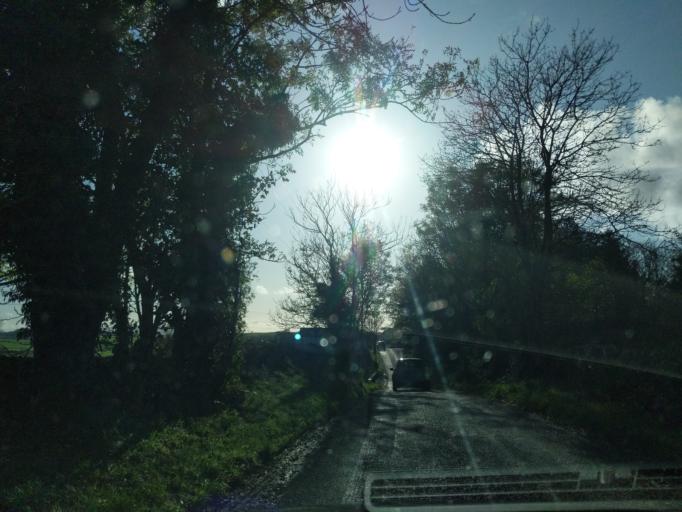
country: GB
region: Scotland
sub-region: Dumfries and Galloway
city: Dalbeattie
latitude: 54.9956
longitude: -3.8348
